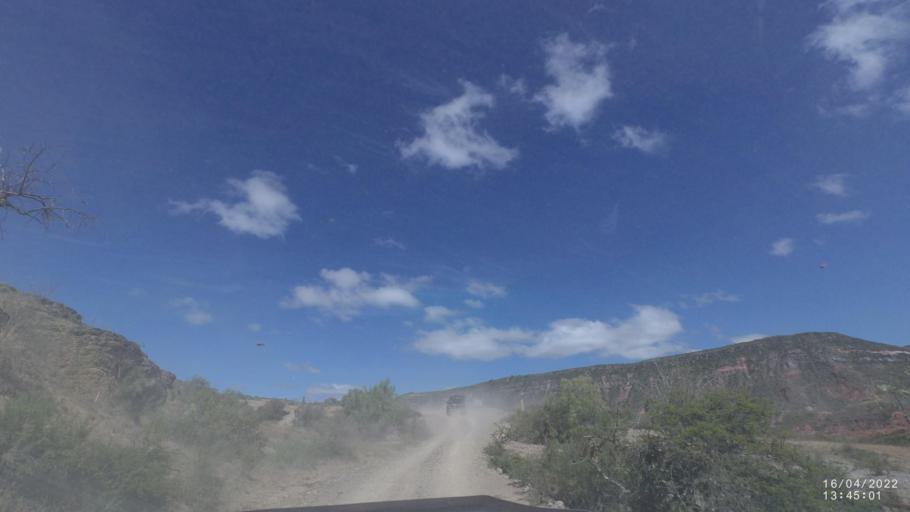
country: BO
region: Cochabamba
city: Mizque
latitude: -18.0014
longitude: -65.5926
